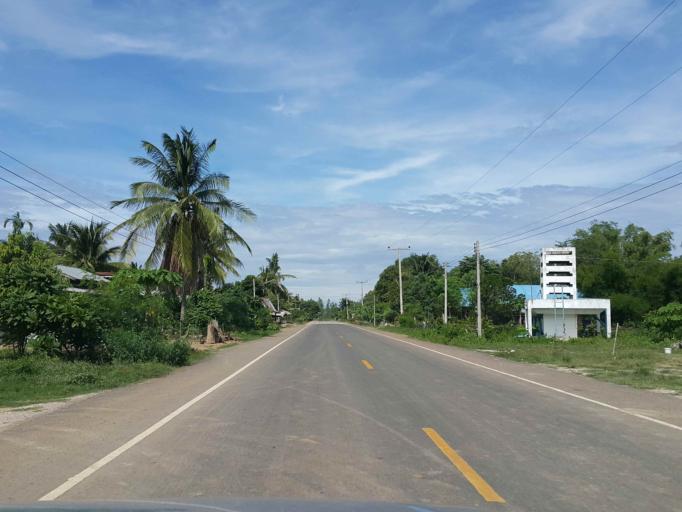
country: TH
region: Sukhothai
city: Ban Dan Lan Hoi
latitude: 17.1138
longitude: 99.5125
